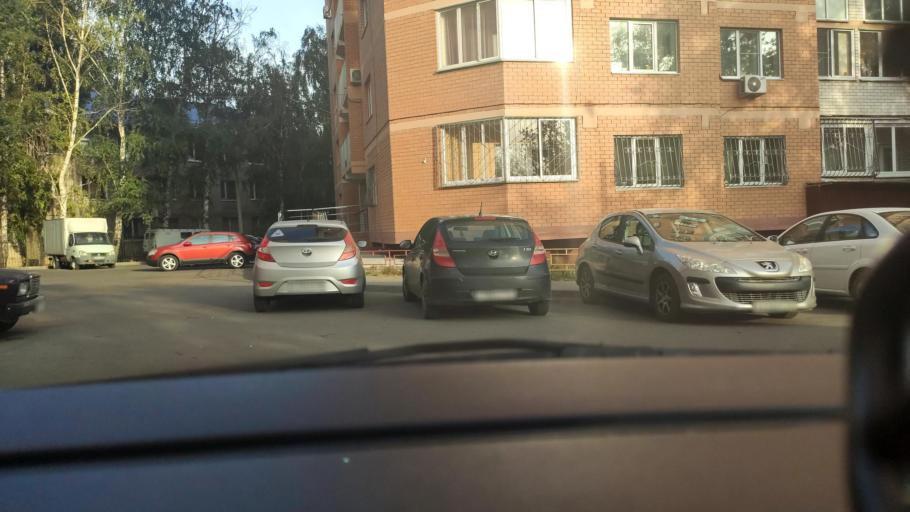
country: RU
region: Voronezj
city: Voronezh
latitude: 51.7015
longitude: 39.2271
